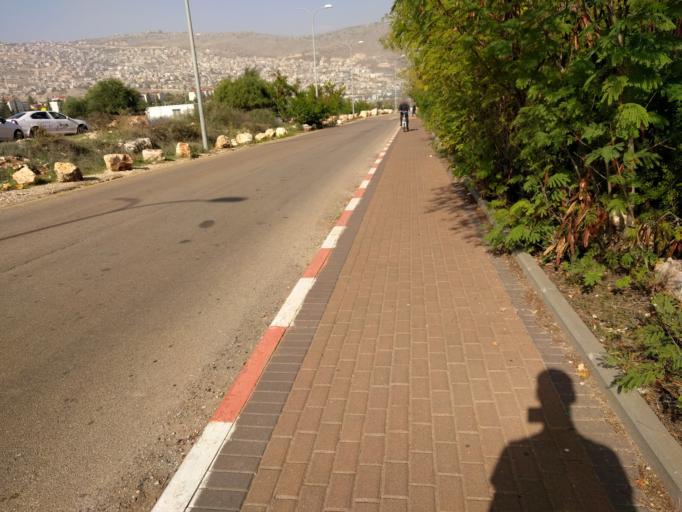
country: IL
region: Northern District
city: Karmi'el
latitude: 32.9111
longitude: 35.2804
